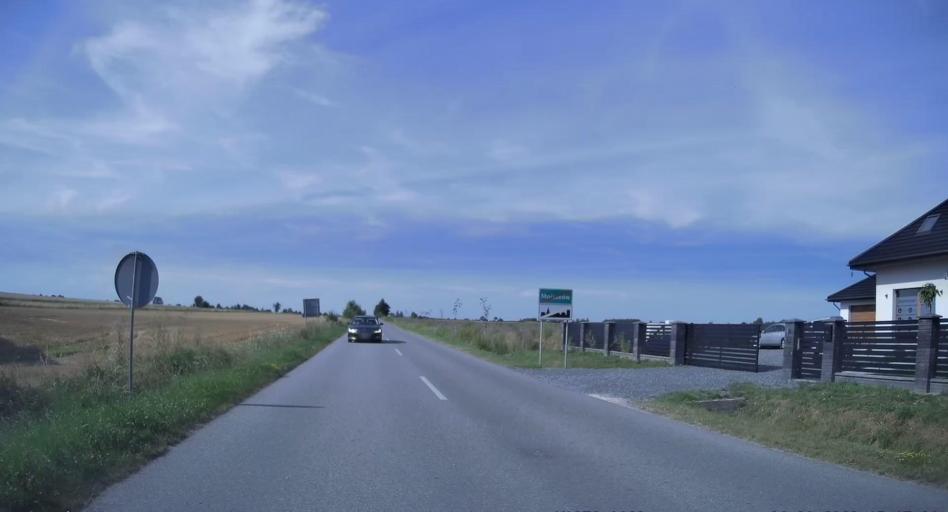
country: PL
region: Lodz Voivodeship
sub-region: Powiat opoczynski
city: Mniszkow
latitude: 51.3776
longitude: 20.0371
